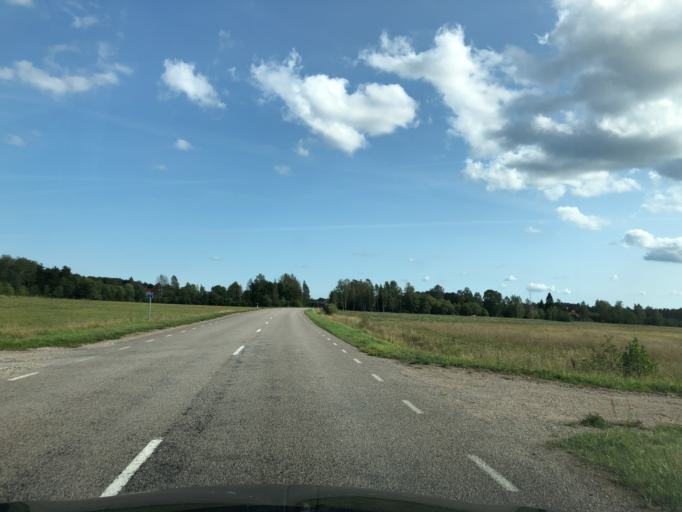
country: EE
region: Hiiumaa
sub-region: Kaerdla linn
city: Kardla
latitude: 58.7166
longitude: 22.5709
